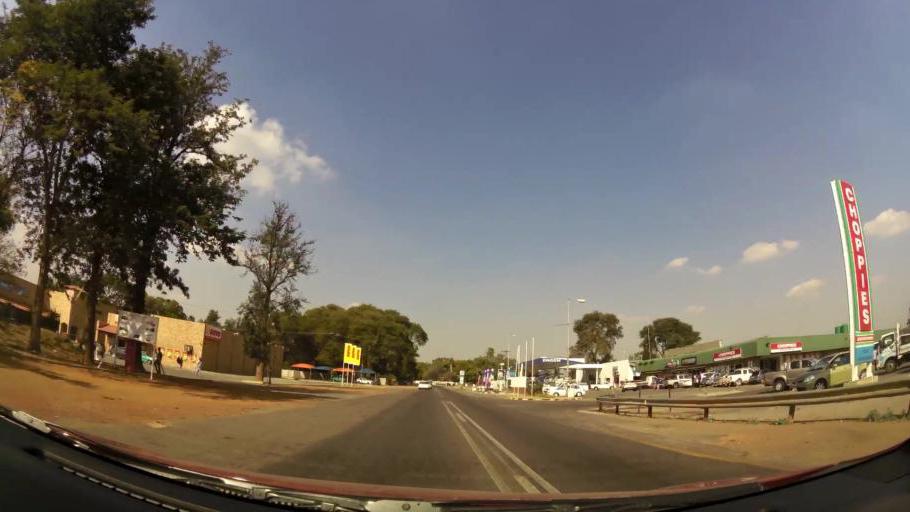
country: ZA
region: North-West
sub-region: Bojanala Platinum District Municipality
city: Rustenburg
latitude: -25.5005
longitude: 27.0905
